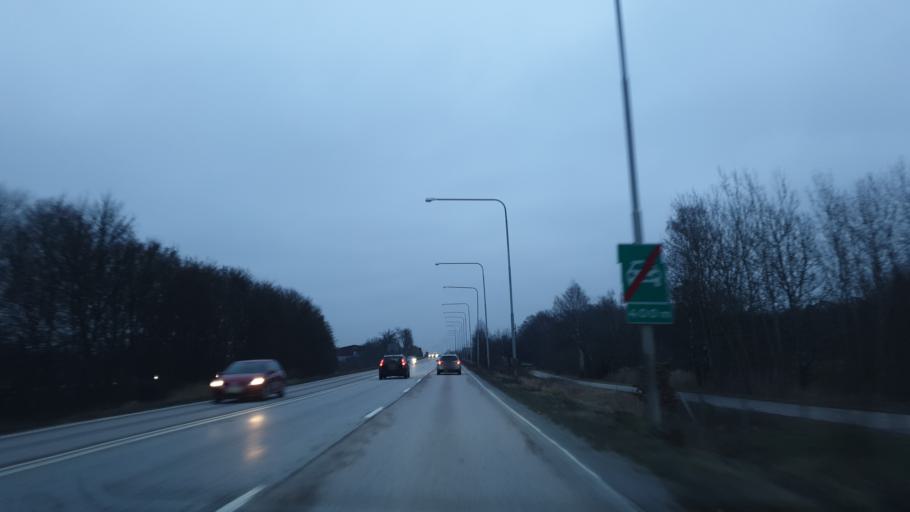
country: SE
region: Blekinge
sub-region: Karlskrona Kommun
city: Karlskrona
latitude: 56.1904
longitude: 15.6228
